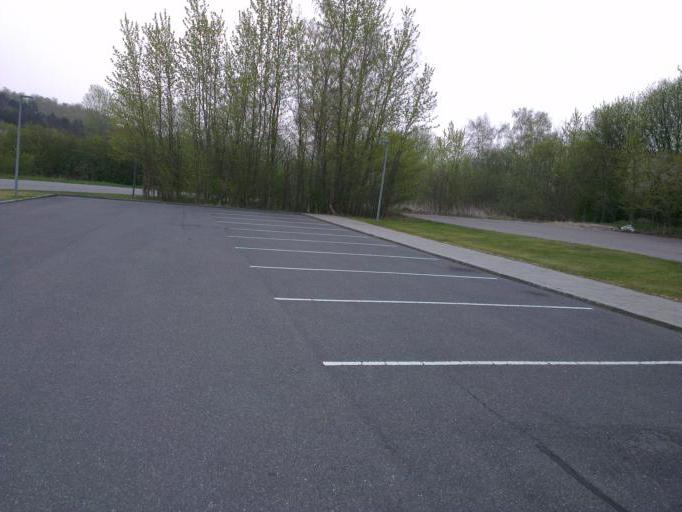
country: DK
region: Capital Region
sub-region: Frederikssund Kommune
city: Frederikssund
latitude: 55.8494
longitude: 12.0872
